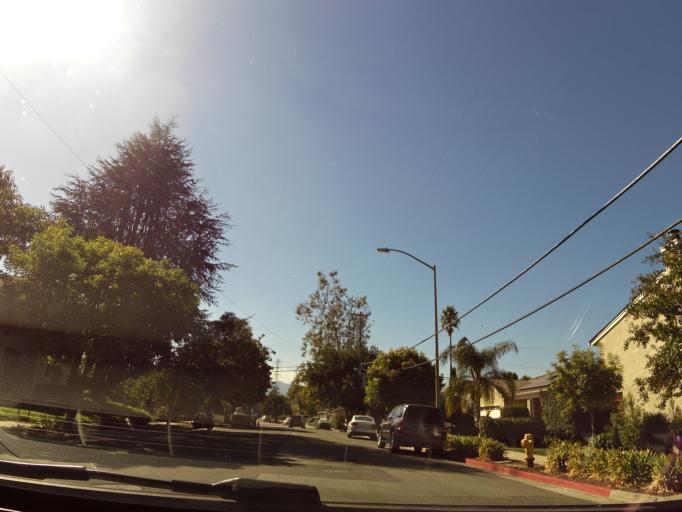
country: US
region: California
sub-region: Santa Clara County
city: Monte Sereno
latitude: 37.2679
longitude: -121.9820
